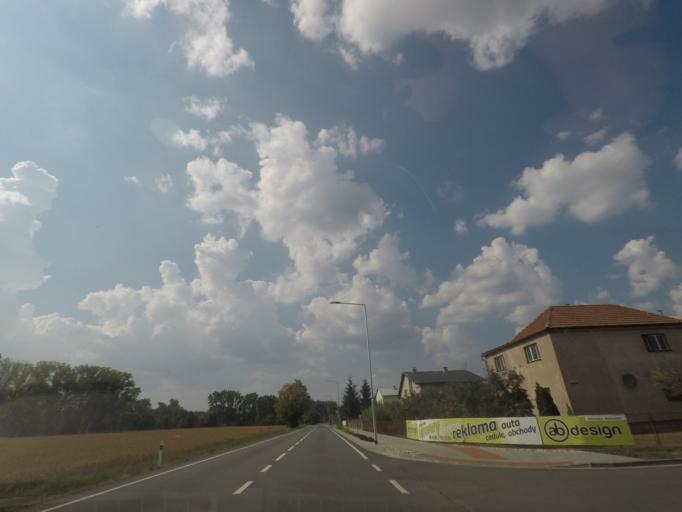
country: CZ
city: Borohradek
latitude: 50.1009
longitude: 16.0887
